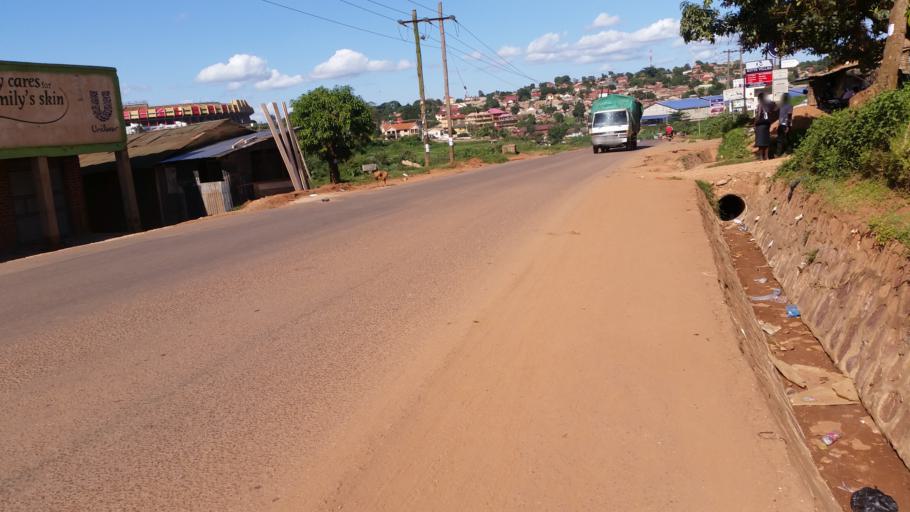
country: UG
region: Central Region
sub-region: Wakiso District
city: Kireka
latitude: 0.3443
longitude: 32.6519
